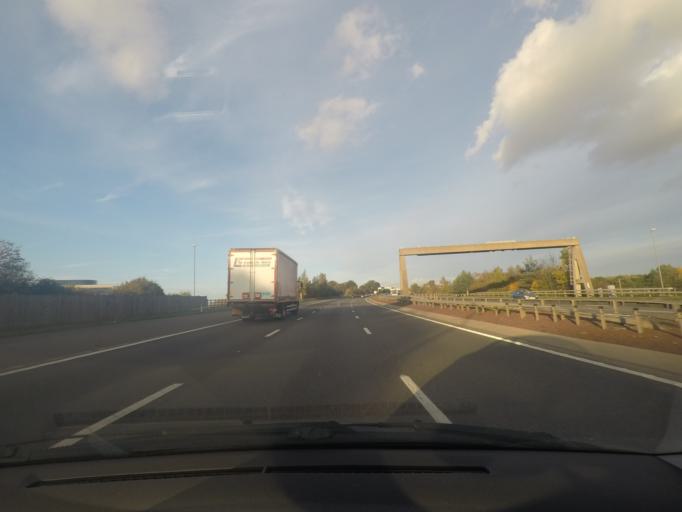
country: GB
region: England
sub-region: City and Borough of Leeds
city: Swillington
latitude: 53.7956
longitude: -1.4236
